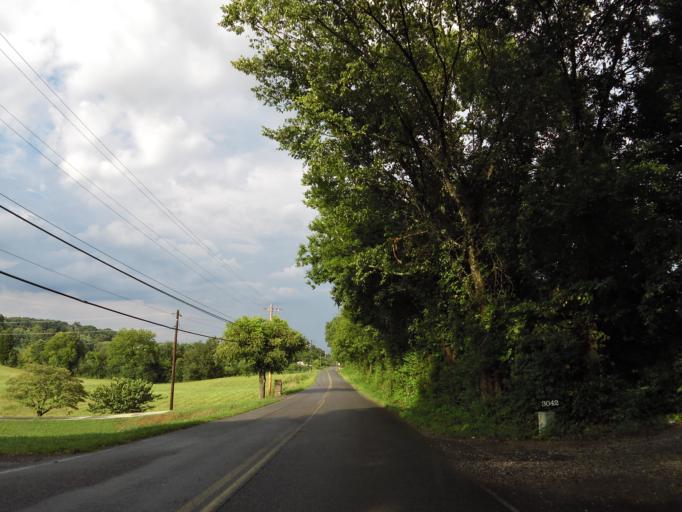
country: US
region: Tennessee
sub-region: Blount County
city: Eagleton Village
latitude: 35.7903
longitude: -83.9185
